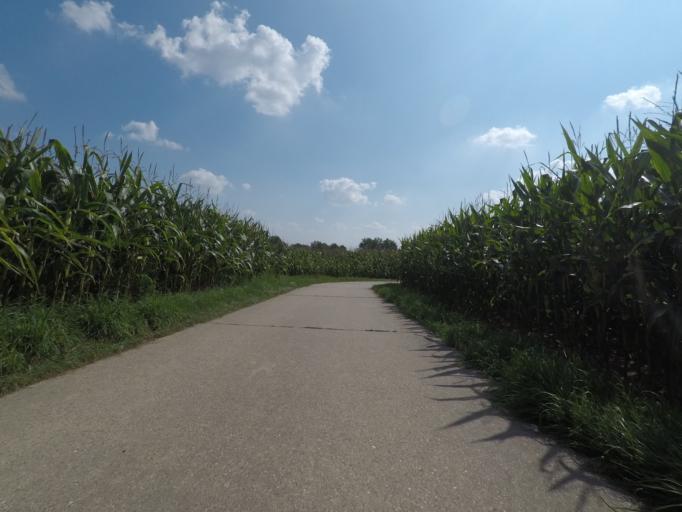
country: DE
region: Baden-Wuerttemberg
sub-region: Regierungsbezirk Stuttgart
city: Ostfildern
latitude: 48.7228
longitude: 9.2596
